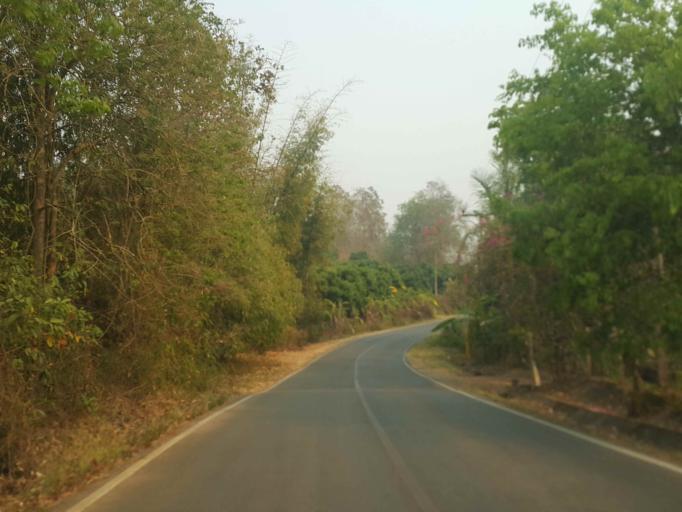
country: TH
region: Chiang Mai
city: Mae Taeng
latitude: 19.1269
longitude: 98.8845
